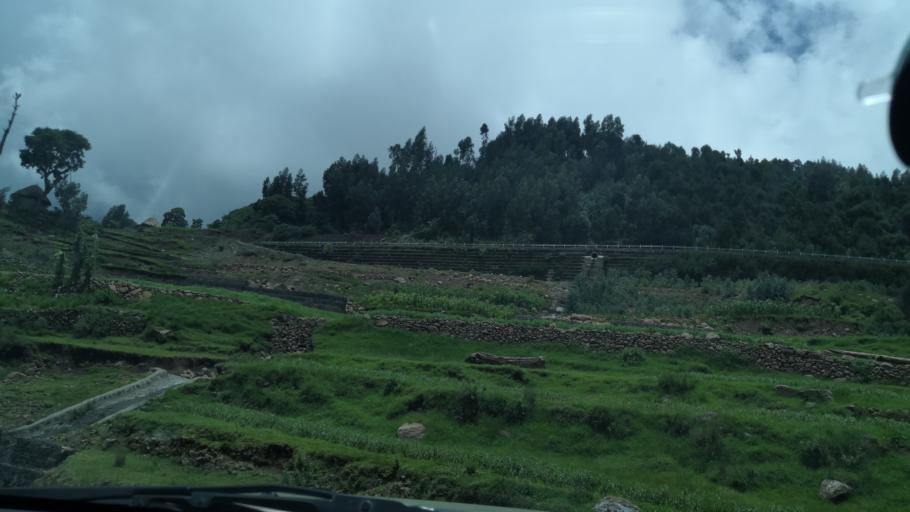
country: ET
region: Amhara
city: Abomsa
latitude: 10.3302
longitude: 39.8414
